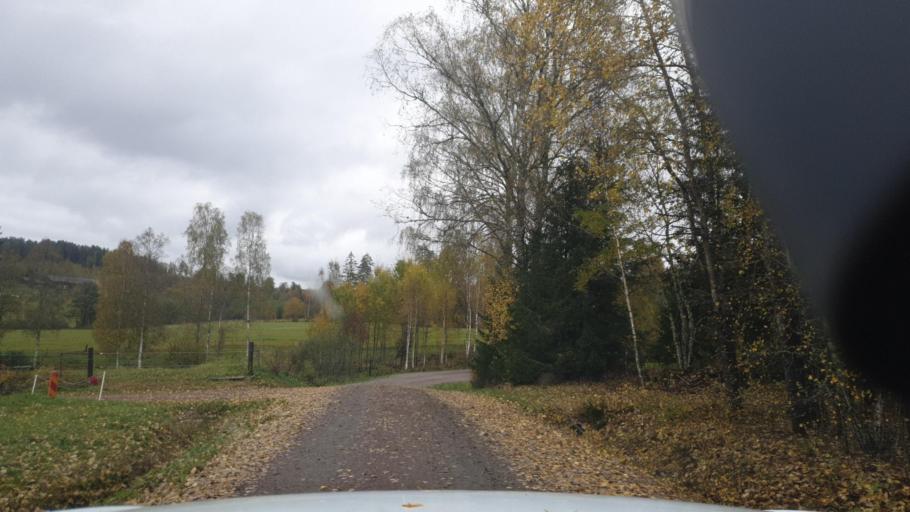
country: SE
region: Vaermland
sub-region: Karlstads Kommun
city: Edsvalla
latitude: 59.4862
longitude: 13.1569
